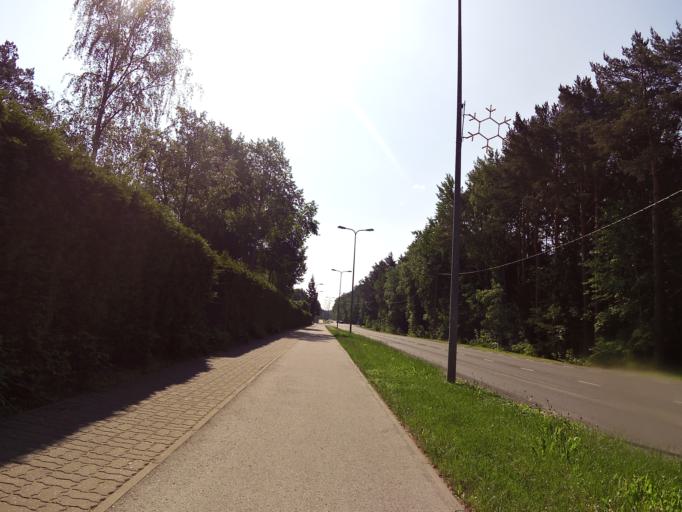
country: EE
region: Harju
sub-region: Harku vald
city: Tabasalu
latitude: 59.4459
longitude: 24.6102
